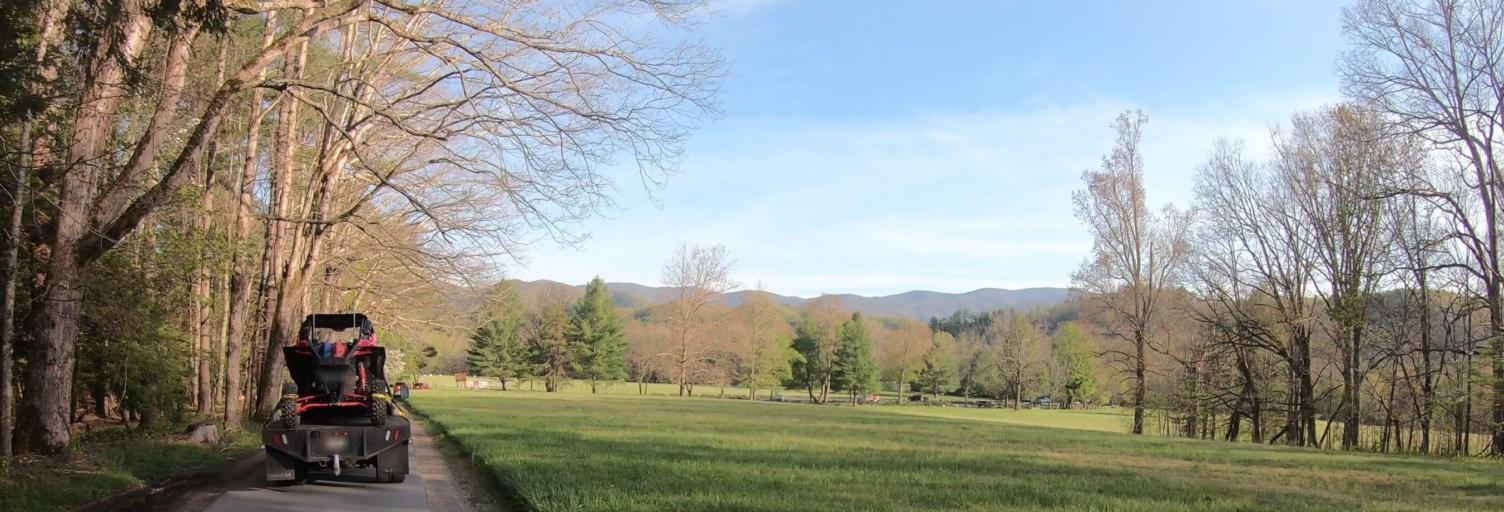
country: US
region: Tennessee
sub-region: Blount County
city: Maryville
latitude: 35.5878
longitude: -83.8418
